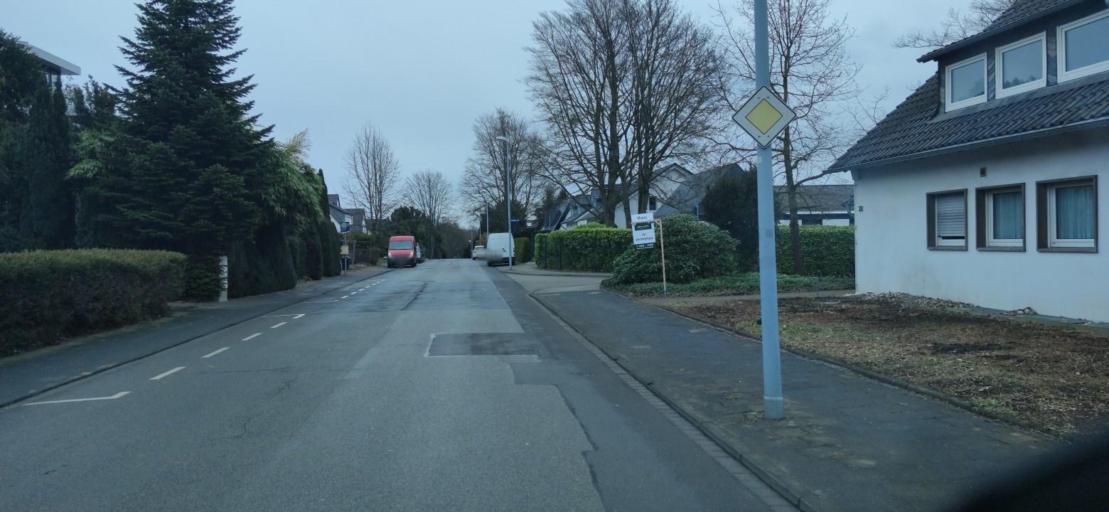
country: DE
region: North Rhine-Westphalia
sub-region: Regierungsbezirk Dusseldorf
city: Muelheim (Ruhr)
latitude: 51.4184
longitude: 6.9107
